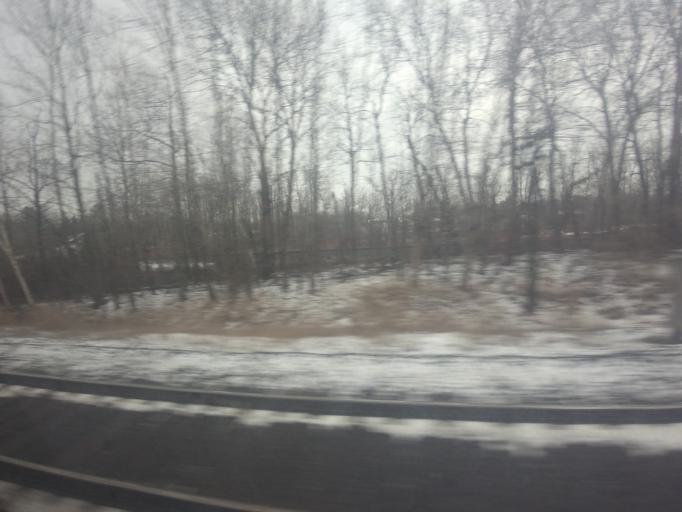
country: CA
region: Ontario
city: Quinte West
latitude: 44.0341
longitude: -77.7483
